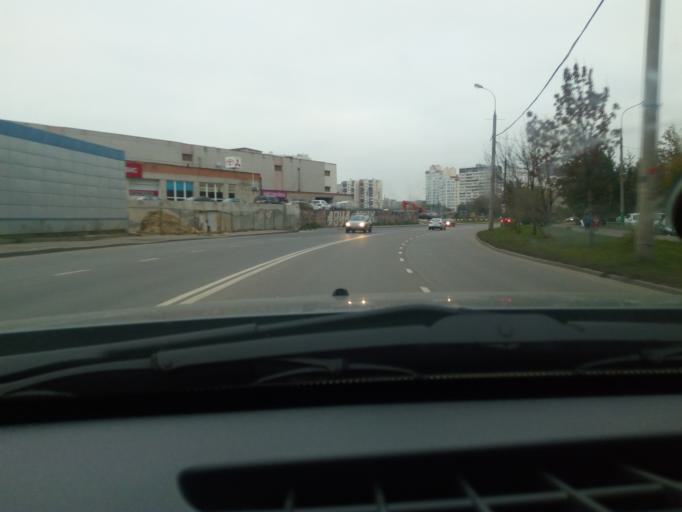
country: RU
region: Moskovskaya
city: Reutov
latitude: 55.7424
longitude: 37.8482
